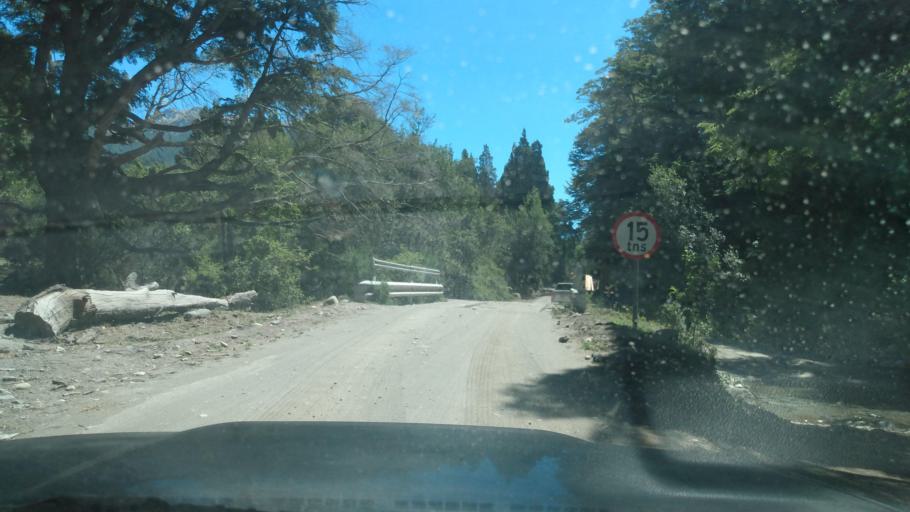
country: AR
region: Neuquen
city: Villa La Angostura
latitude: -40.6287
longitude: -71.4856
